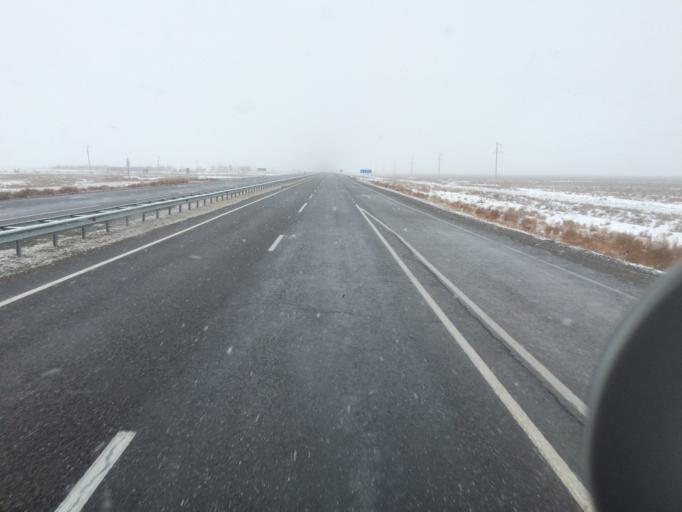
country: KZ
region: Ongtustik Qazaqstan
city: Turkestan
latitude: 43.4581
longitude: 67.9319
